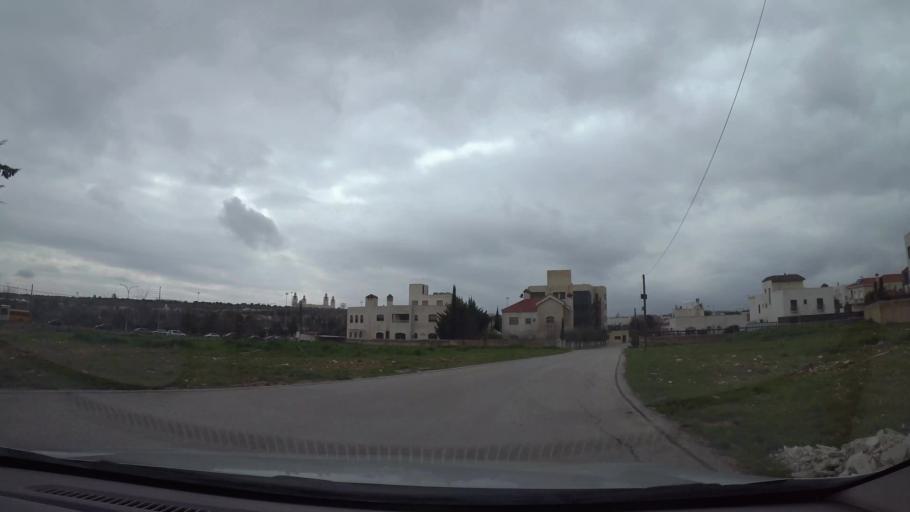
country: JO
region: Amman
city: Wadi as Sir
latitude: 31.9910
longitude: 35.8320
